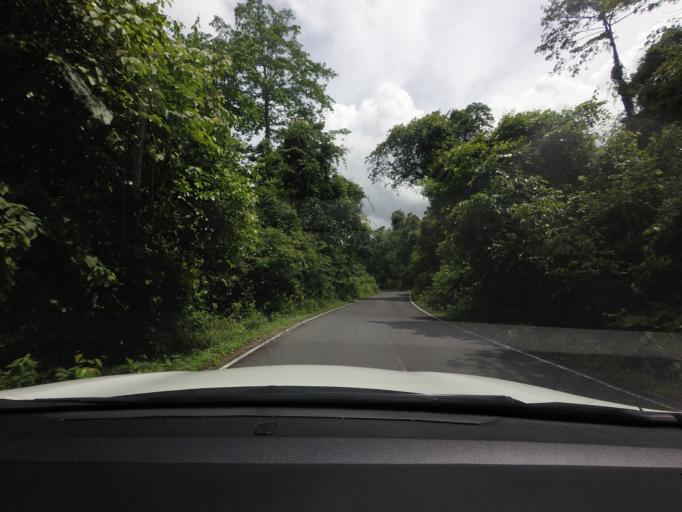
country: TH
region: Nakhon Nayok
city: Pak Phli
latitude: 14.3337
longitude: 101.3554
